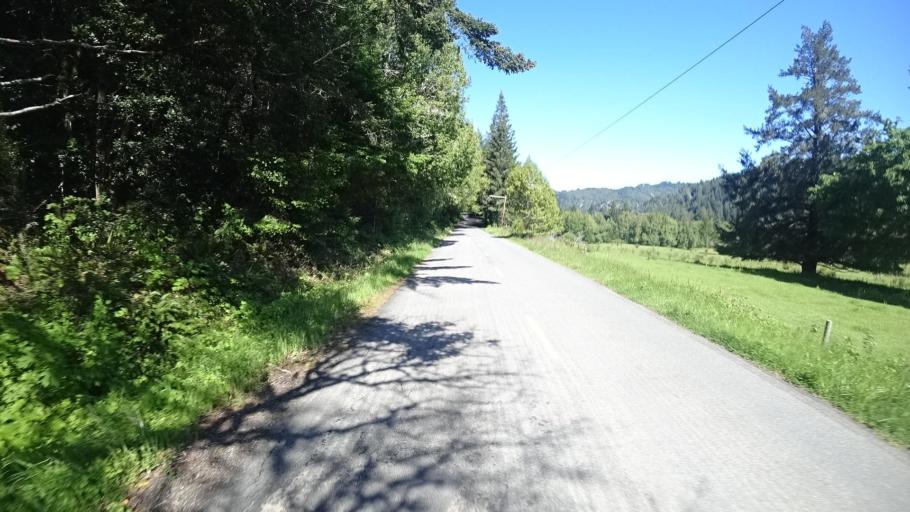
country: US
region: California
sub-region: Humboldt County
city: Rio Dell
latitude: 40.2678
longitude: -124.2012
